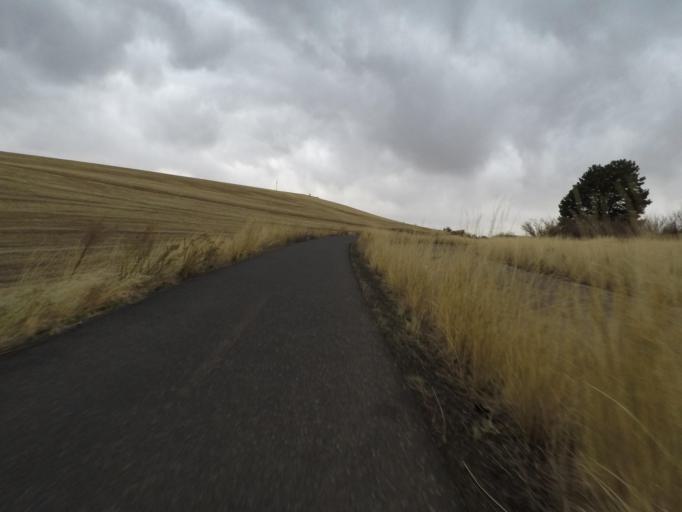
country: US
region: Washington
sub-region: Walla Walla County
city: Walla Walla East
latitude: 46.0707
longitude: -118.2703
